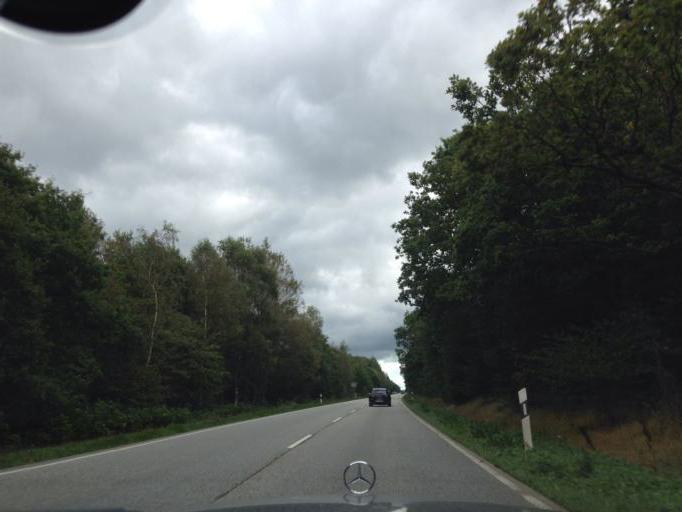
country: DE
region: Schleswig-Holstein
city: Leck
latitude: 54.7513
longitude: 9.0104
